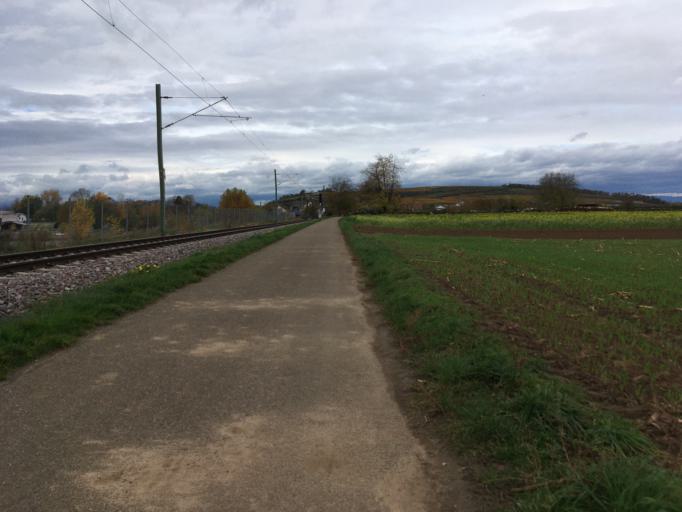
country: DE
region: Baden-Wuerttemberg
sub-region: Freiburg Region
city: Sasbach
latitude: 48.1400
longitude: 7.6289
